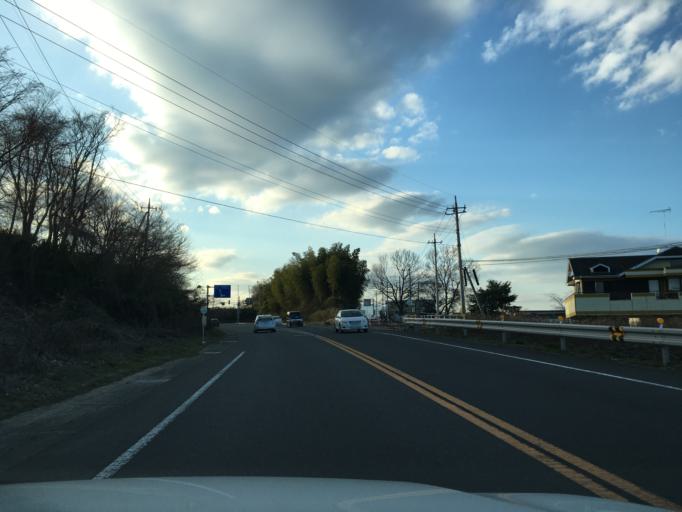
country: JP
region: Tochigi
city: Otawara
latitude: 36.8639
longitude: 140.0838
